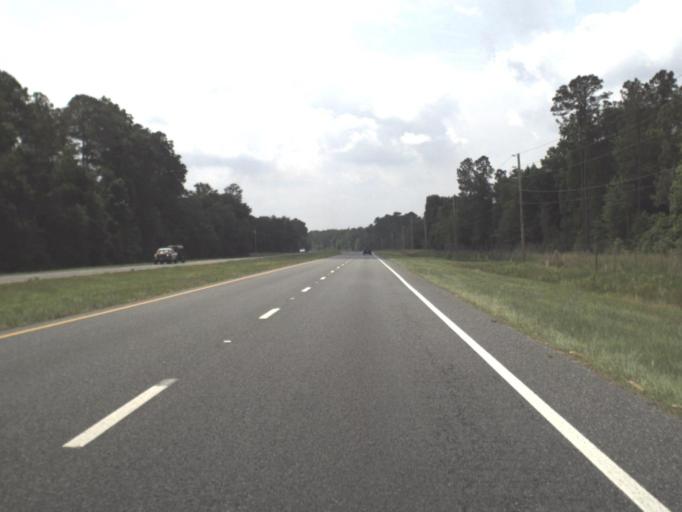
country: US
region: Florida
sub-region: Putnam County
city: Palatka
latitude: 29.8191
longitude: -81.6606
